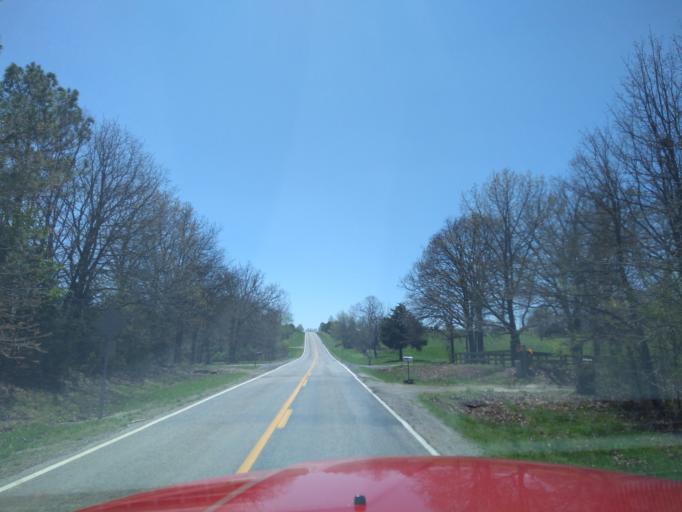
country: US
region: Arkansas
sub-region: Washington County
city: West Fork
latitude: 35.8308
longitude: -94.2666
